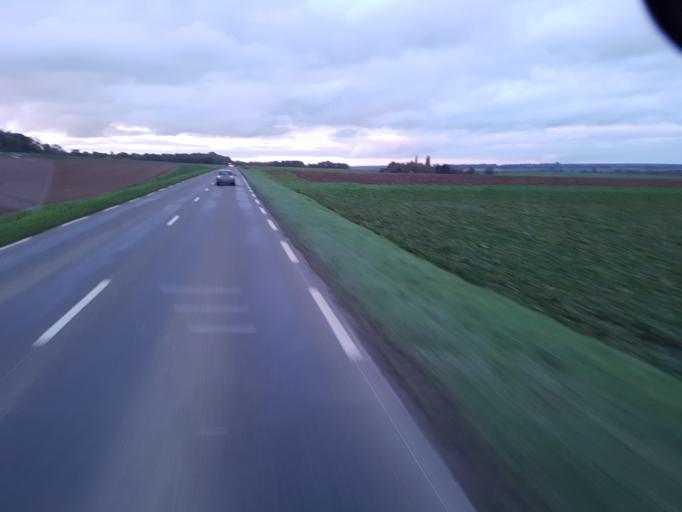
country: FR
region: Picardie
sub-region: Departement de l'Aisne
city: Coincy
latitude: 49.1620
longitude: 3.3812
